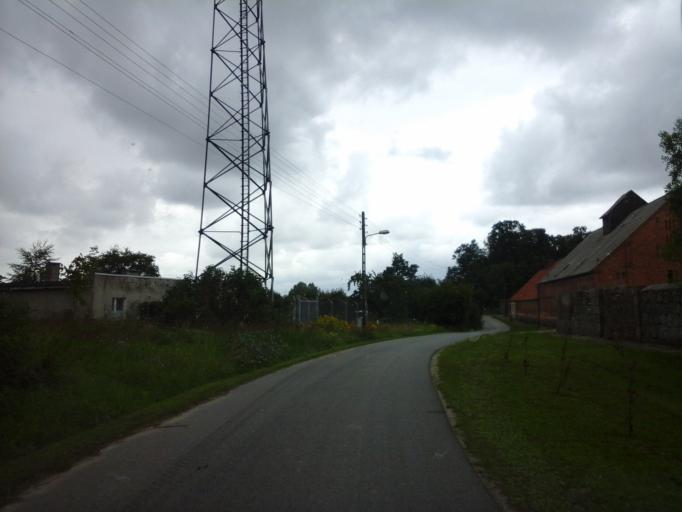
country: PL
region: West Pomeranian Voivodeship
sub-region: Powiat choszczenski
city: Krzecin
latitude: 53.0050
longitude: 15.4211
